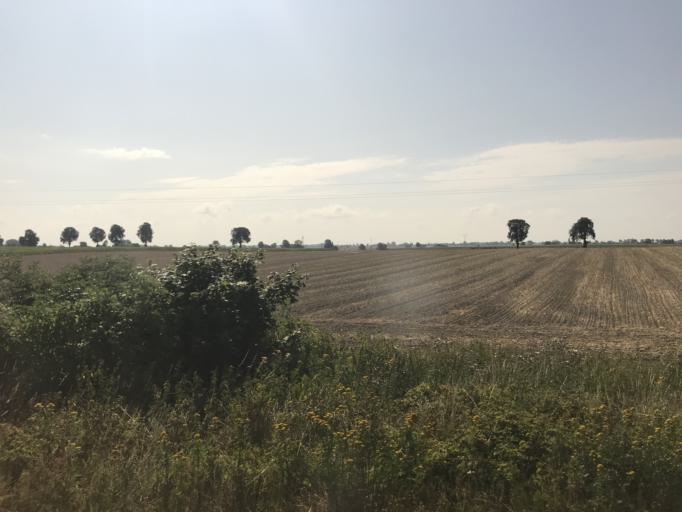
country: PL
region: Kujawsko-Pomorskie
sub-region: Powiat swiecki
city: Pruszcz
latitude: 53.3111
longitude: 18.1623
